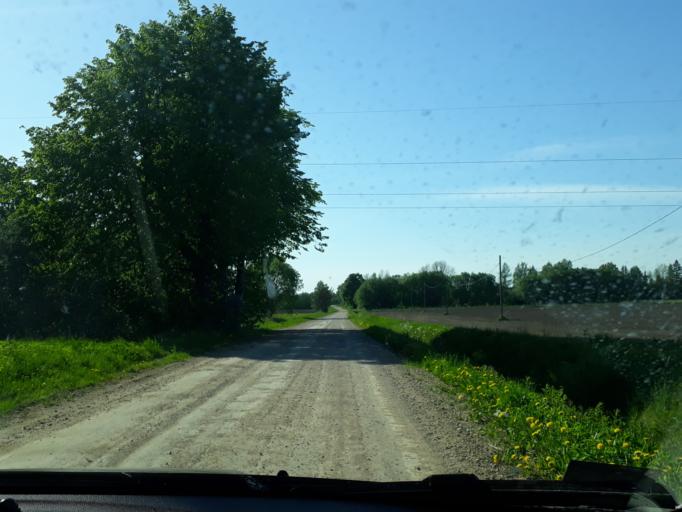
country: EE
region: Paernumaa
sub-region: Tootsi vald
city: Tootsi
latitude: 58.5832
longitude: 24.9050
